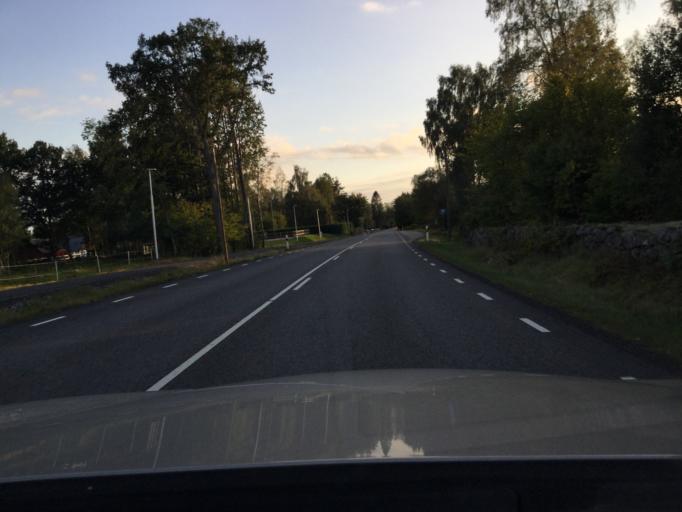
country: SE
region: Kronoberg
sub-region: Almhults Kommun
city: AElmhult
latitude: 56.6562
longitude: 14.2495
